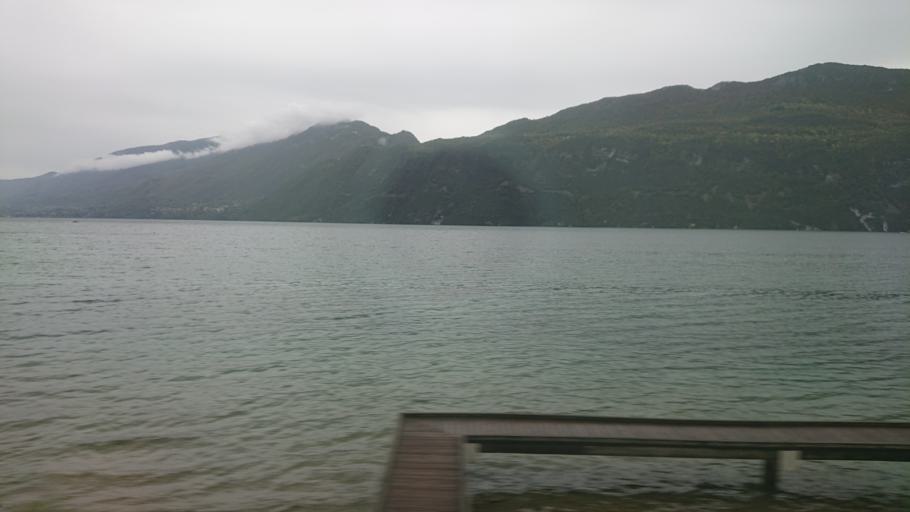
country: FR
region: Rhone-Alpes
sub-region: Departement de la Savoie
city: Brison-Saint-Innocent
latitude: 45.7164
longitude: 5.8866
